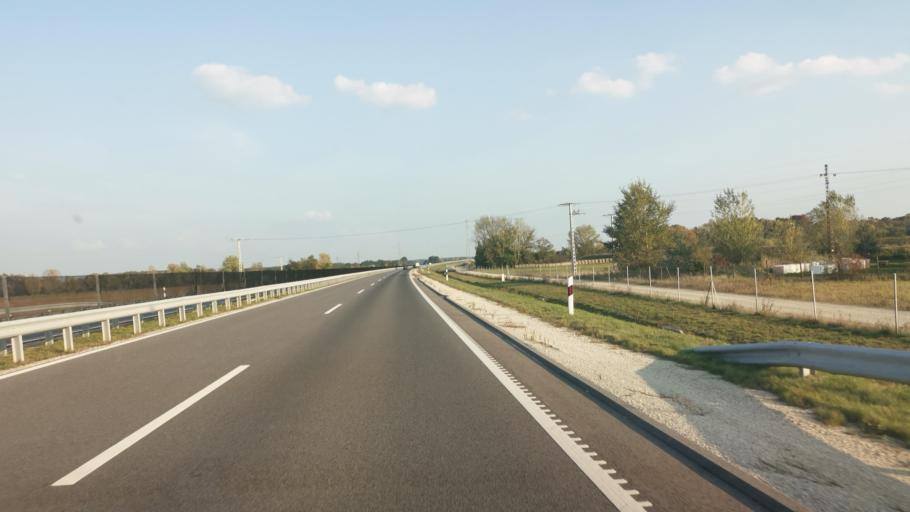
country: HU
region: Gyor-Moson-Sopron
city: Kapuvar
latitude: 47.5810
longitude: 16.9836
